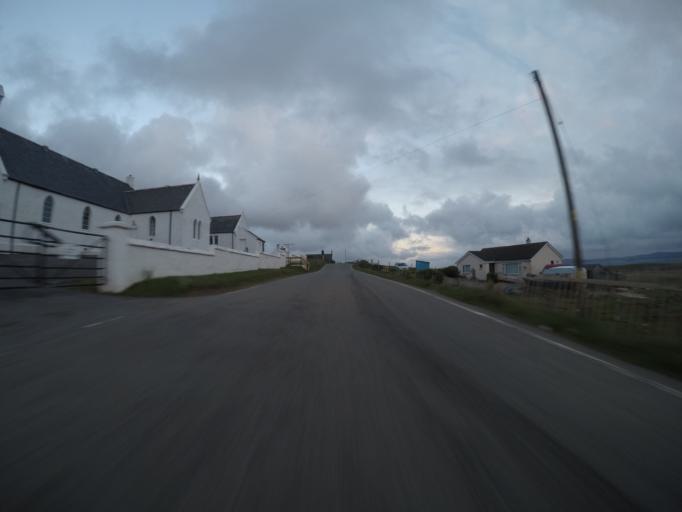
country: GB
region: Scotland
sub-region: Highland
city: Portree
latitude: 57.6386
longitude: -6.3764
